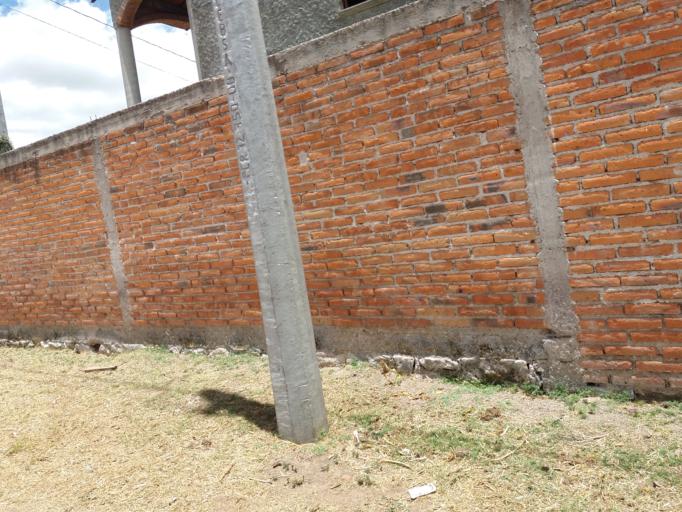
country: MX
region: Aguascalientes
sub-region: Aguascalientes
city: San Sebastian [Fraccionamiento]
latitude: 21.7789
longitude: -102.2622
